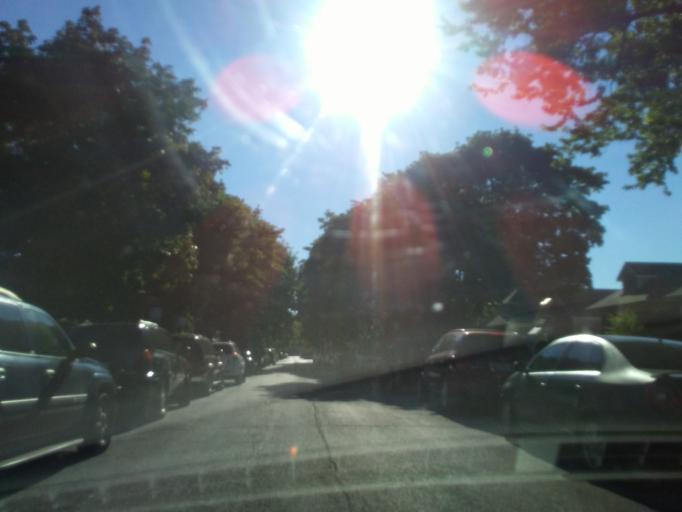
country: US
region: Illinois
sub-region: Cook County
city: Oak Park
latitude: 41.9263
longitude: -87.7425
